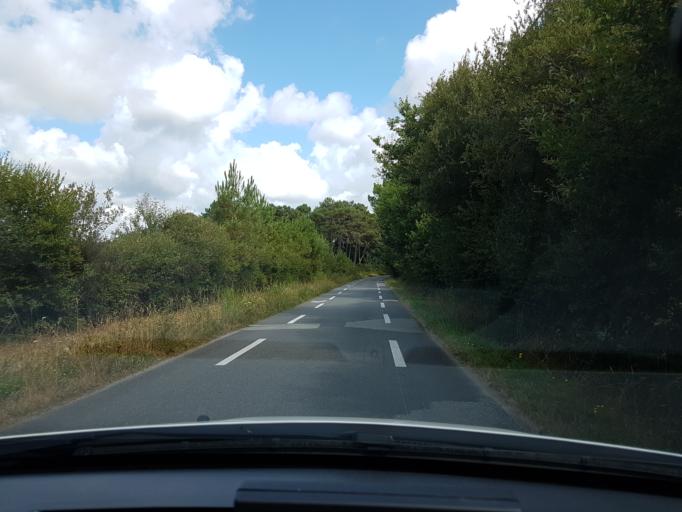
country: FR
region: Brittany
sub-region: Departement du Morbihan
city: Sainte-Helene
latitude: 47.7128
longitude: -3.1945
